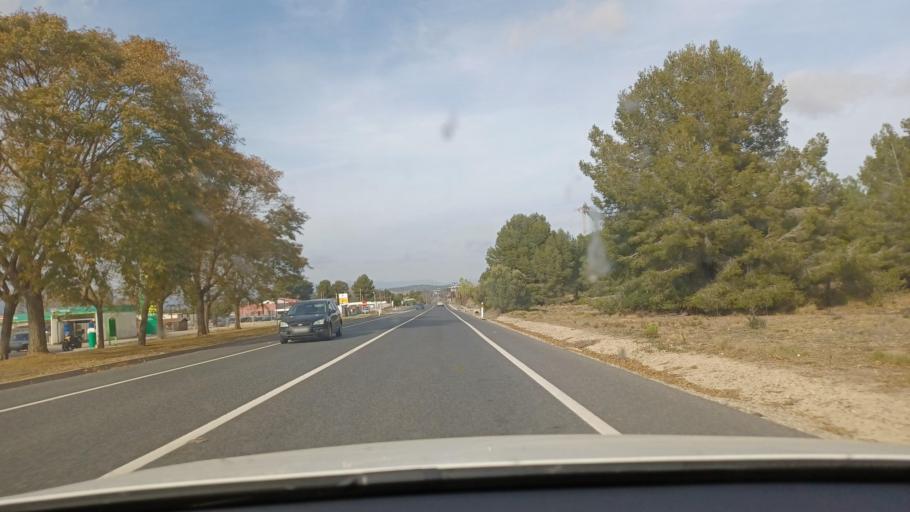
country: ES
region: Catalonia
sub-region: Provincia de Tarragona
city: la Pobla de Mafumet
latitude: 41.1731
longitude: 1.2400
